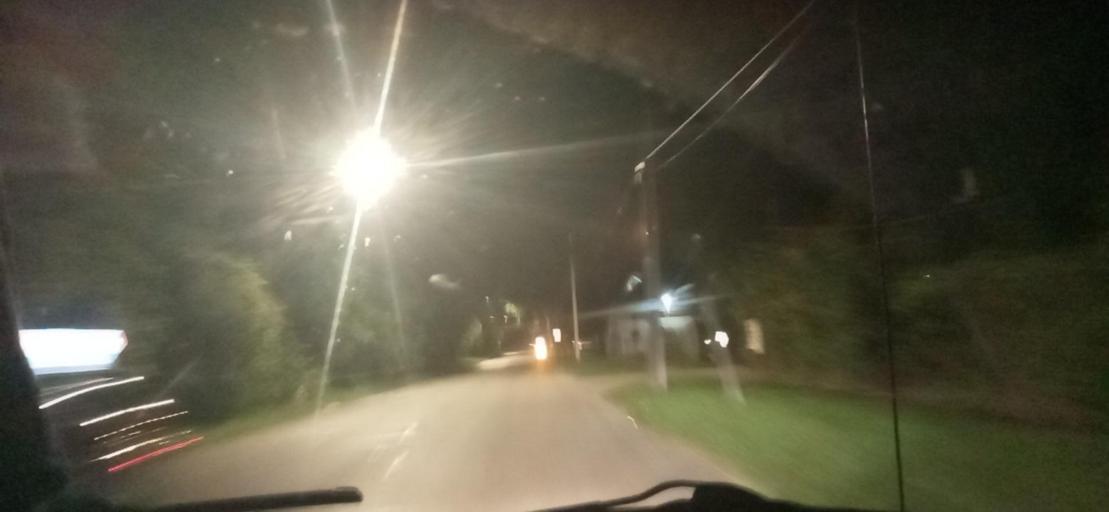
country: US
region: Ohio
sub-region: Summit County
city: Akron
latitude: 41.0650
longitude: -81.5085
